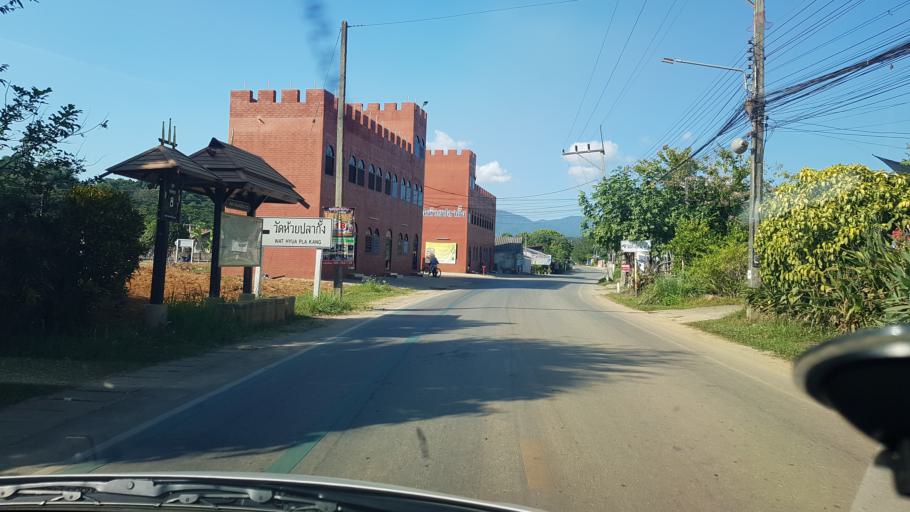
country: TH
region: Chiang Rai
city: Chiang Rai
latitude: 19.9494
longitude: 99.8097
